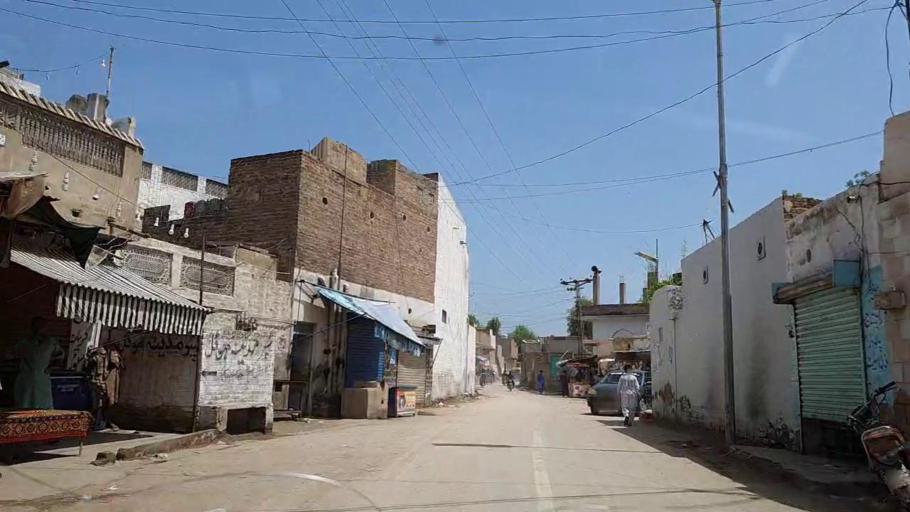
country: PK
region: Sindh
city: Naushahro Firoz
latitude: 26.8375
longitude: 68.1228
